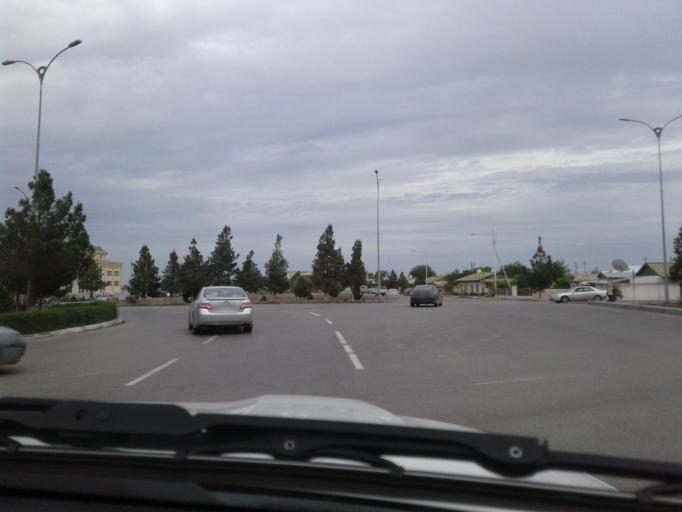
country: TM
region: Mary
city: Mary
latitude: 37.5942
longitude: 61.8765
